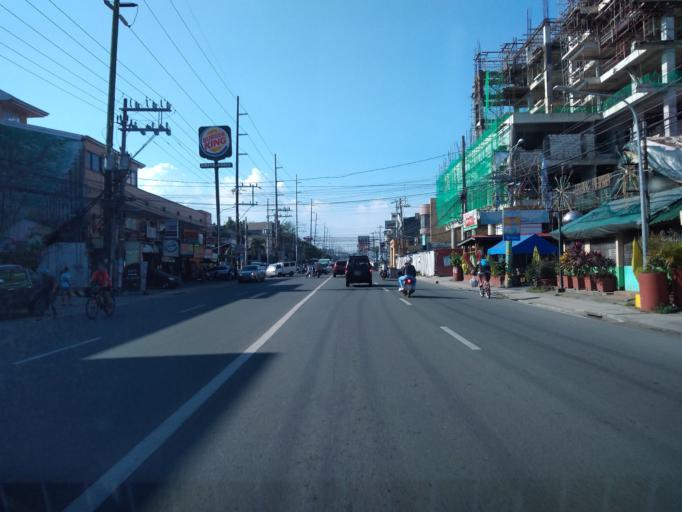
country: PH
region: Calabarzon
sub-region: Province of Laguna
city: Calamba
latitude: 14.1935
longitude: 121.1656
